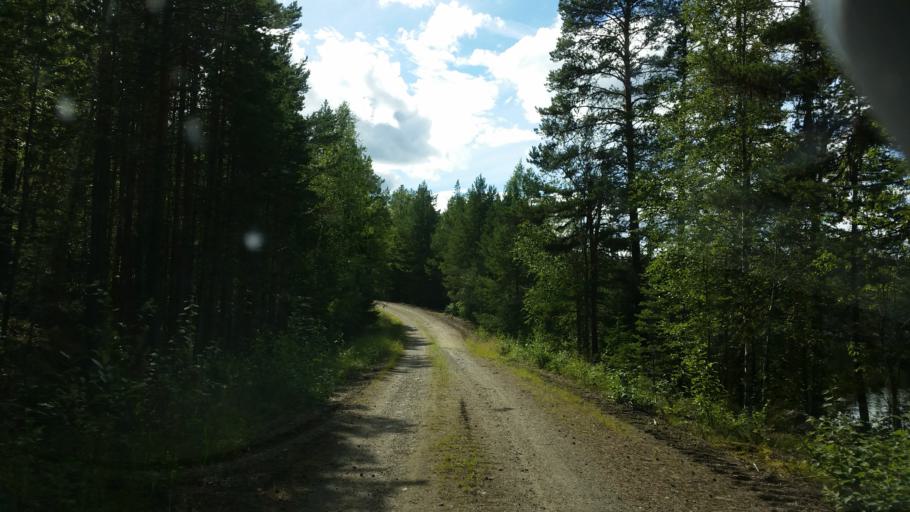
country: SE
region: Vaesternorrland
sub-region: Ange Kommun
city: Ange
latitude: 62.2343
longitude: 15.7115
